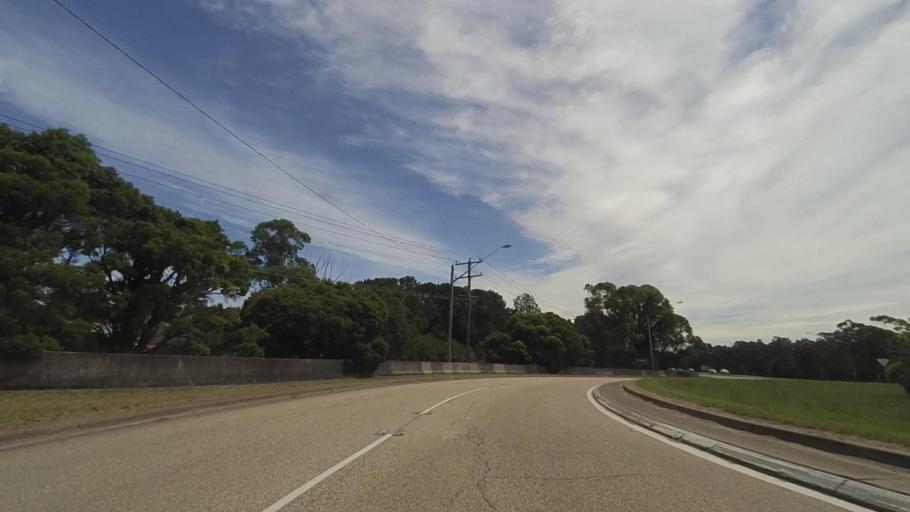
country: AU
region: New South Wales
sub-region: Port Stephens Shire
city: Medowie
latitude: -32.7893
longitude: 151.9035
